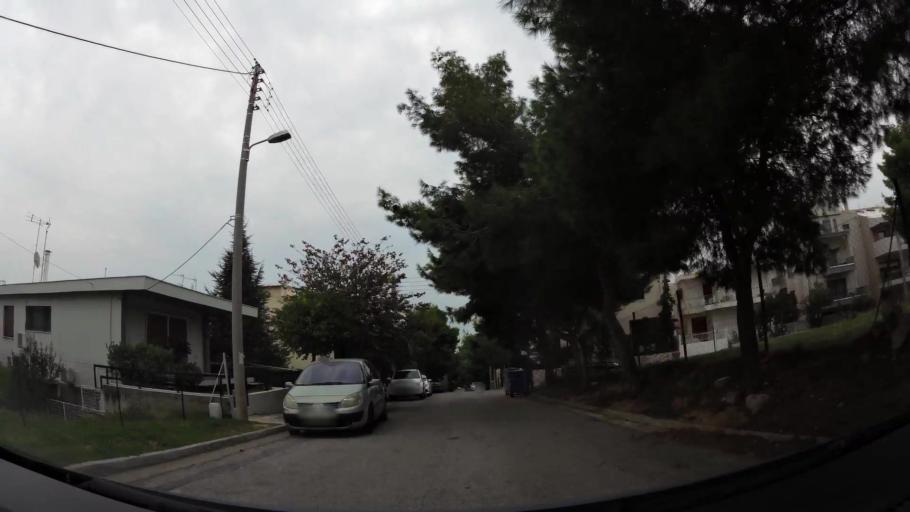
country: GR
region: Attica
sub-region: Nomarchia Athinas
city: Alimos
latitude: 37.9136
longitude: 23.7326
